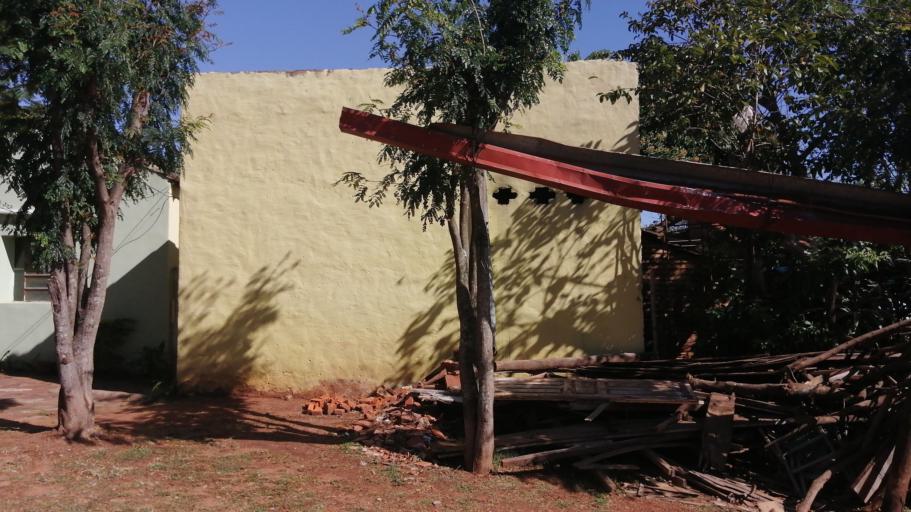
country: PY
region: Misiones
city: San Juan Bautista
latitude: -26.6656
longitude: -57.1387
